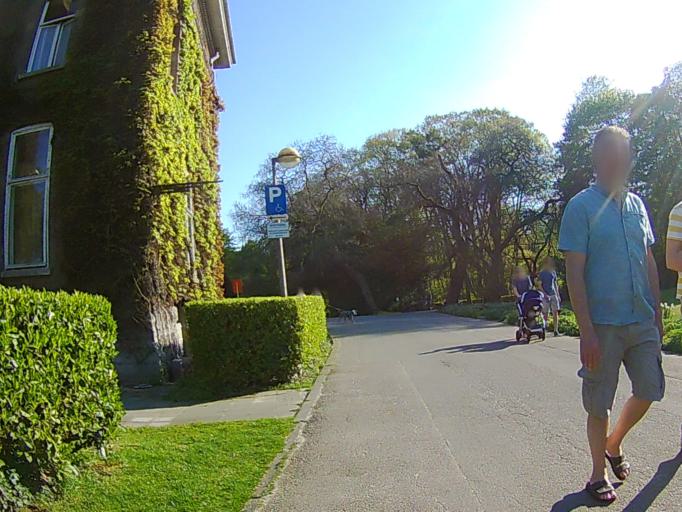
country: BE
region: Flanders
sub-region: Provincie Antwerpen
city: Borsbeek
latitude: 51.2187
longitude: 4.4724
